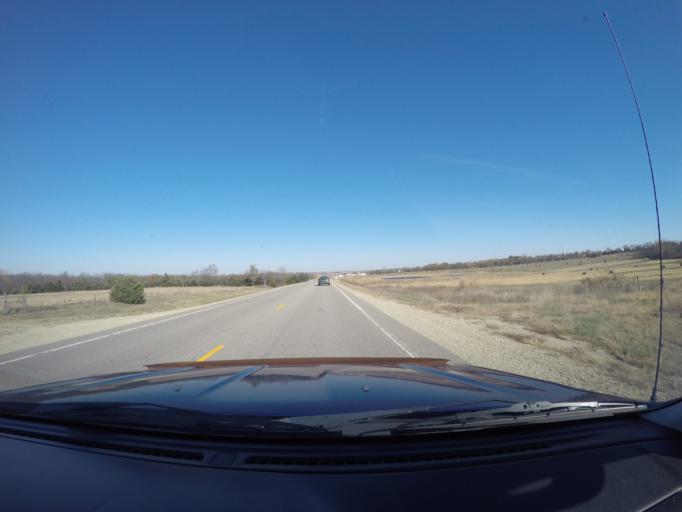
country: US
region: Kansas
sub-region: Marshall County
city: Blue Rapids
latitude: 39.4238
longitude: -96.7644
